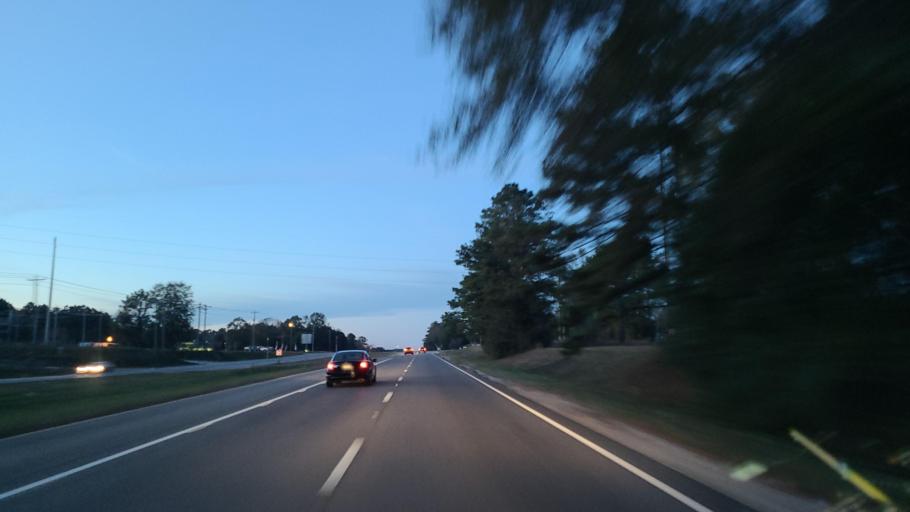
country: US
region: Mississippi
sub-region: Forrest County
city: Hattiesburg
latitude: 31.2200
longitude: -89.2652
